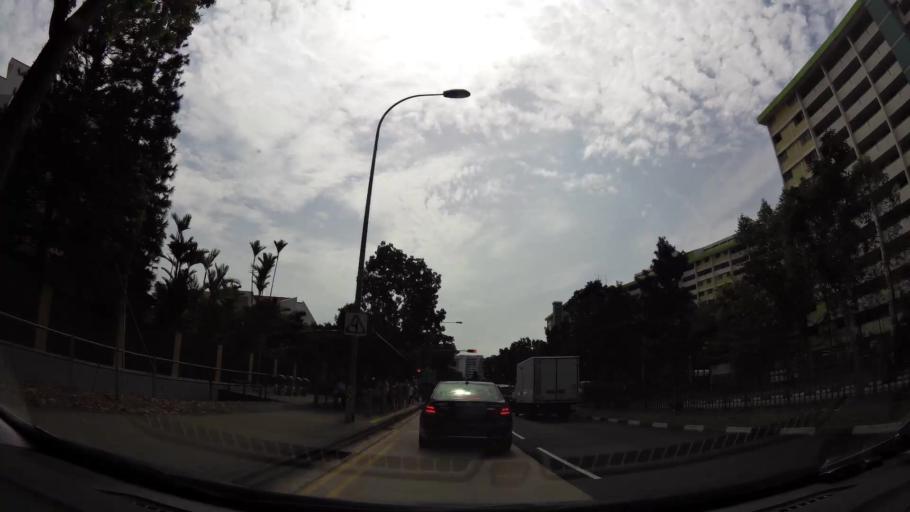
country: SG
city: Singapore
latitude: 1.3079
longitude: 103.7619
